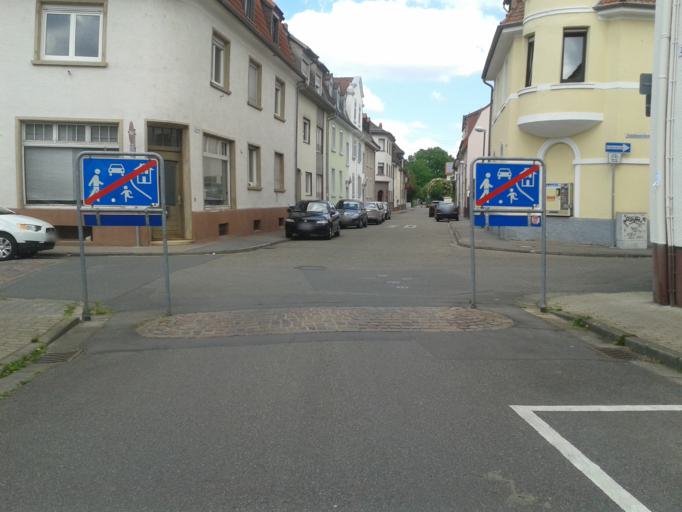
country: DE
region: Baden-Wuerttemberg
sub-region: Karlsruhe Region
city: Heidelberg
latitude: 49.3812
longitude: 8.6692
